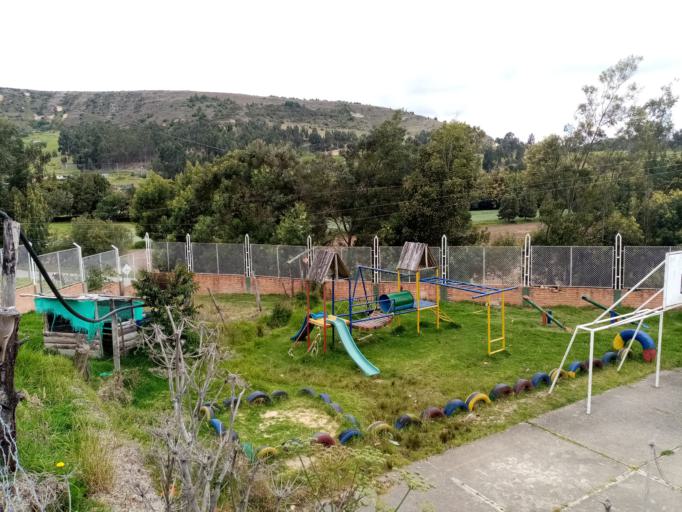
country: CO
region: Boyaca
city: Siachoque
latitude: 5.5689
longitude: -73.2620
